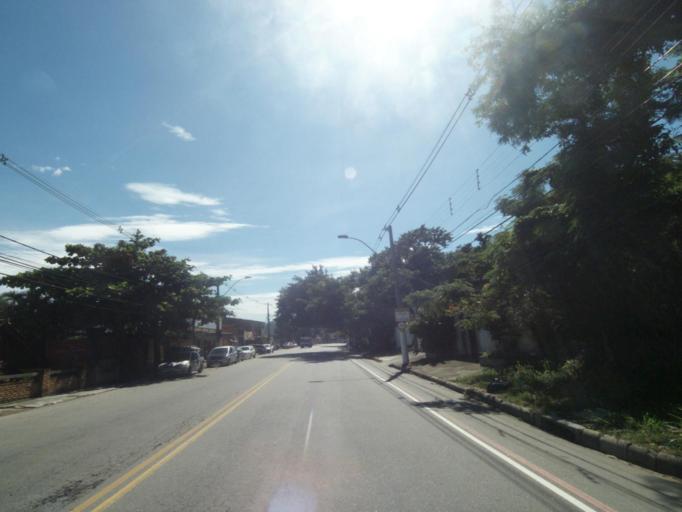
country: BR
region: Rio de Janeiro
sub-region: Niteroi
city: Niteroi
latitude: -22.9528
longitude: -43.0653
